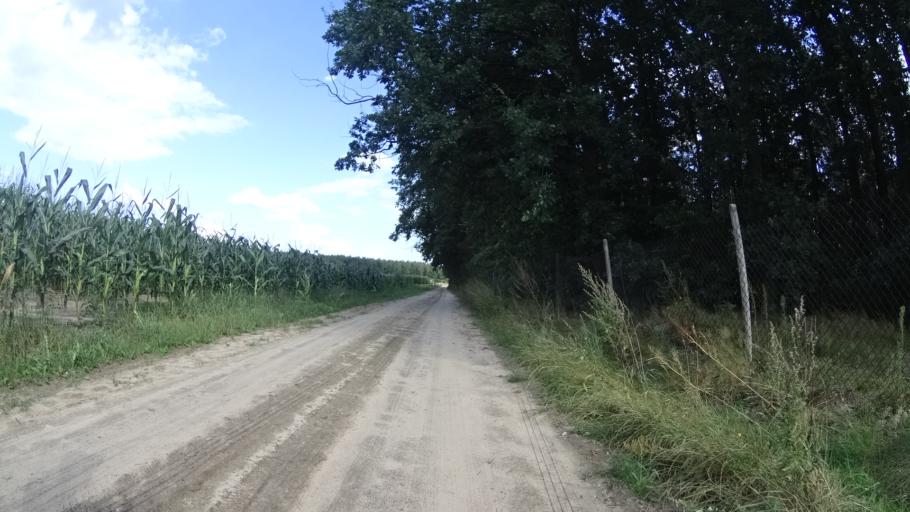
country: PL
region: Masovian Voivodeship
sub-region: Powiat grojecki
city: Mogielnica
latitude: 51.6773
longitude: 20.7725
